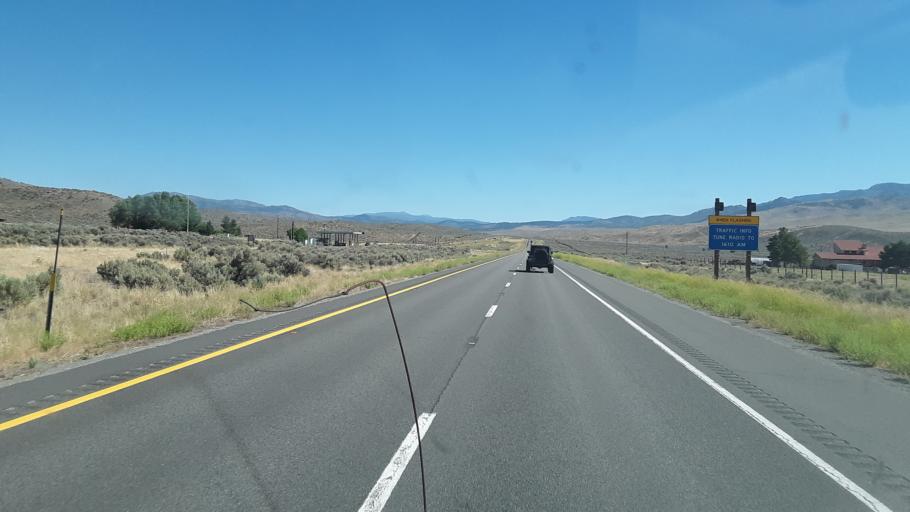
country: US
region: Nevada
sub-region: Washoe County
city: Cold Springs
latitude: 39.7334
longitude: -120.0392
